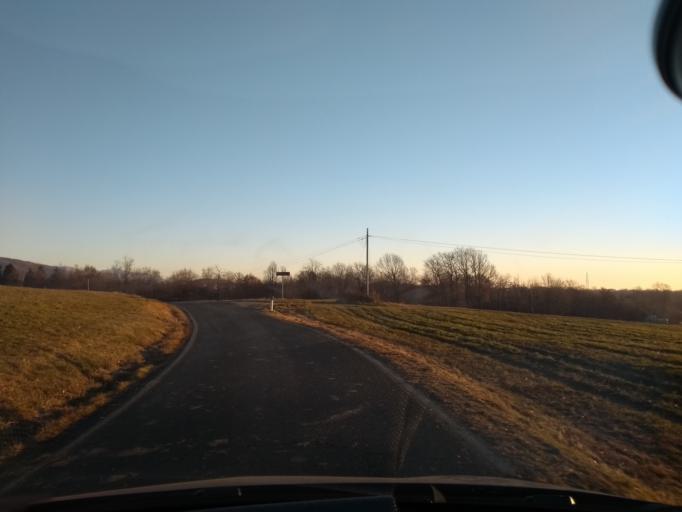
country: IT
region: Piedmont
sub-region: Provincia di Torino
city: Mathi
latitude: 45.2799
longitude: 7.5425
